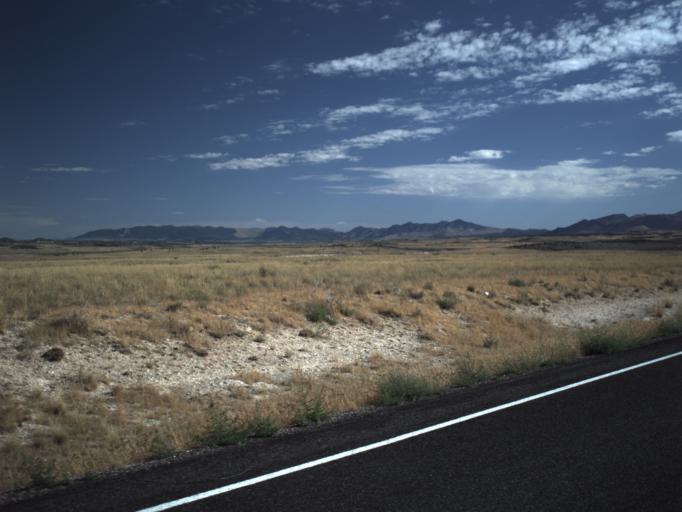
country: US
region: Utah
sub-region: Juab County
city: Mona
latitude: 39.7009
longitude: -112.2196
